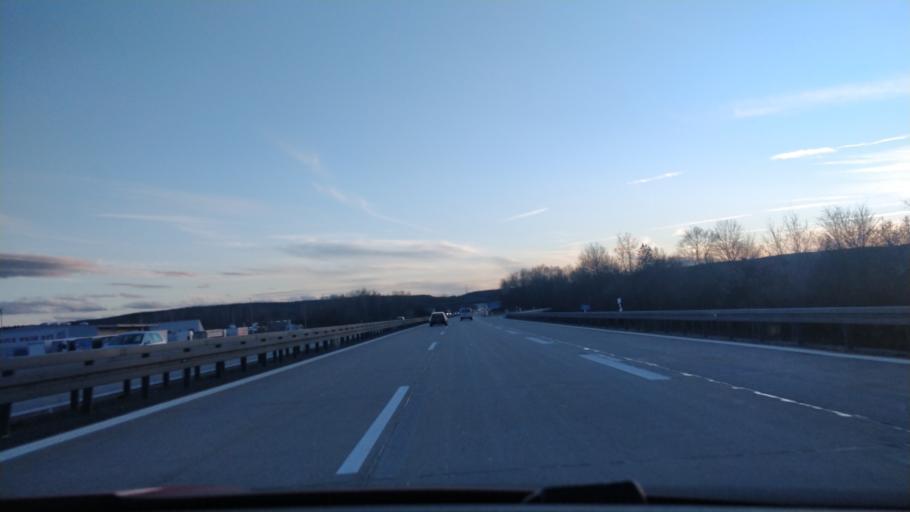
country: DE
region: Bavaria
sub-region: Upper Palatinate
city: Luhe-Wildenau
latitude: 49.5964
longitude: 12.1446
